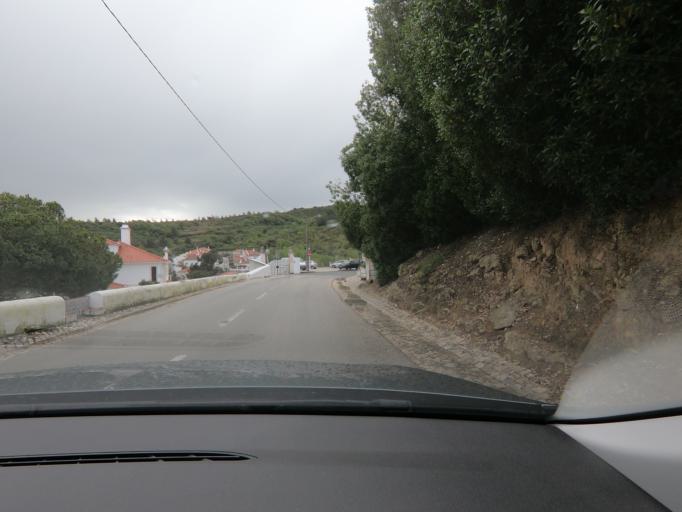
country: PT
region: Lisbon
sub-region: Alenquer
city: Alenquer
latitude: 39.0528
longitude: -9.0101
